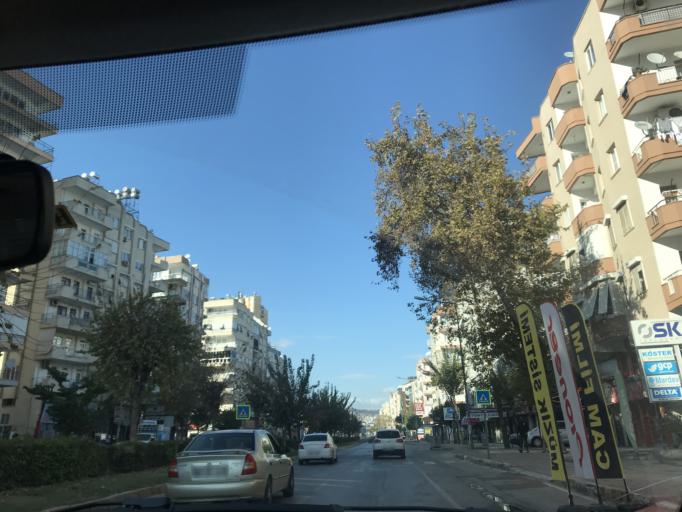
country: TR
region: Antalya
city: Antalya
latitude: 36.9051
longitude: 30.7005
